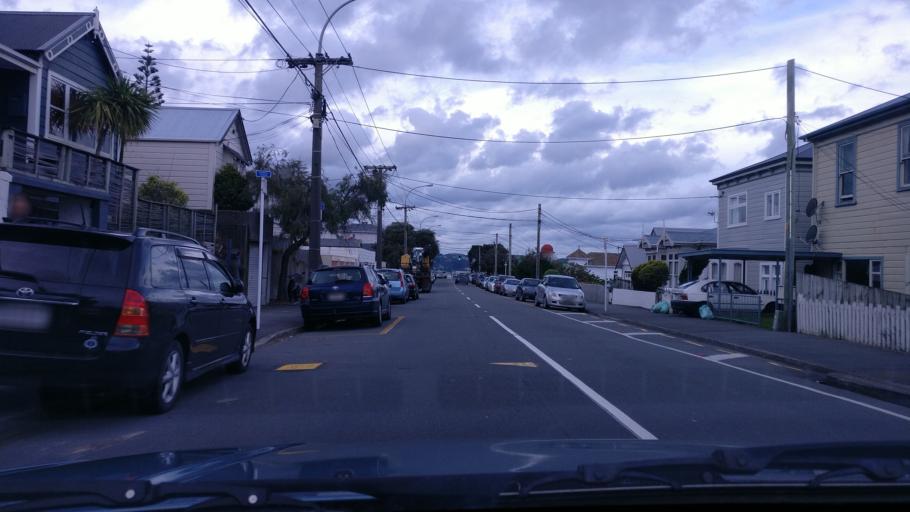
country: NZ
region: Wellington
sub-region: Wellington City
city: Wellington
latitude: -41.3122
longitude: 174.7764
